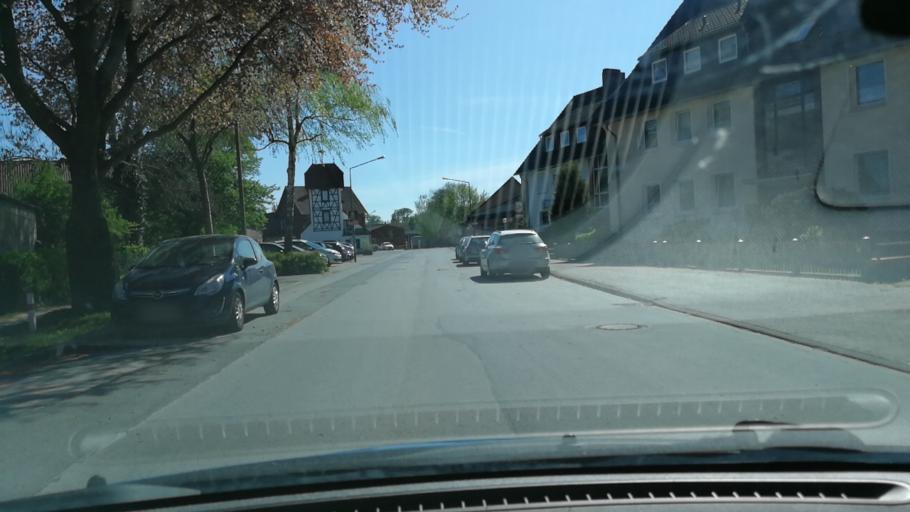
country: DE
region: Lower Saxony
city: Lehrte
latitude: 52.3656
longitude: 9.9120
